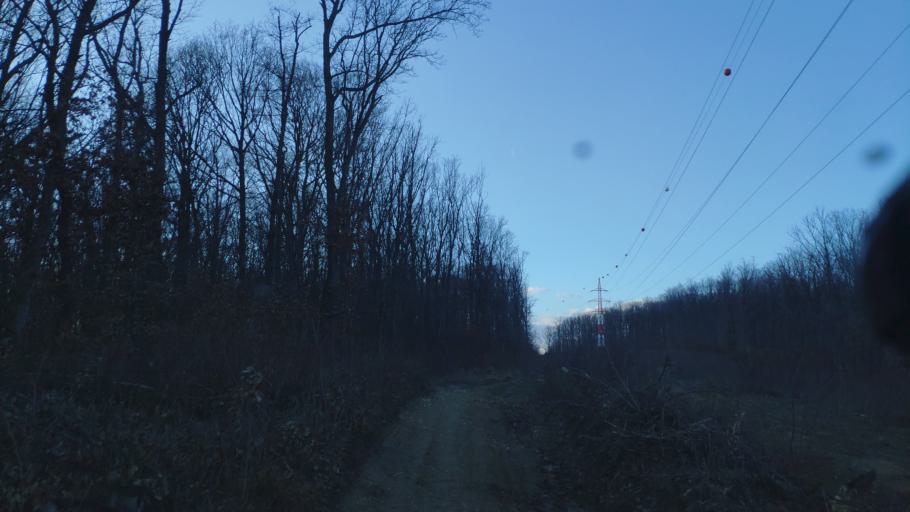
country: SK
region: Kosicky
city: Kosice
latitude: 48.6937
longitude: 21.1815
